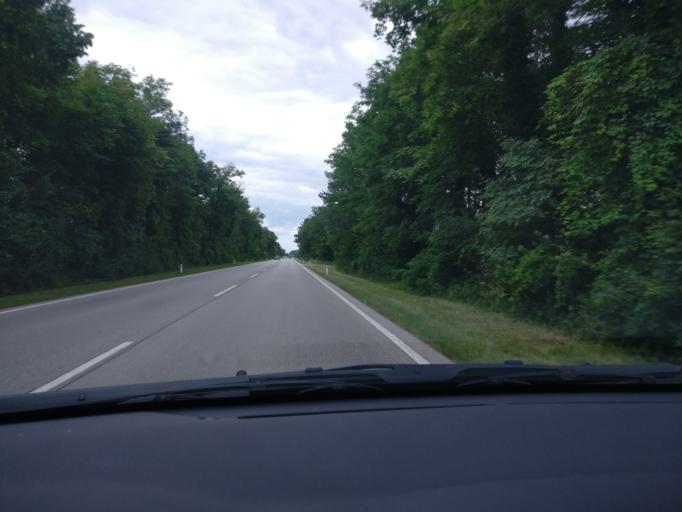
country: AT
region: Lower Austria
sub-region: Wiener Neustadt Stadt
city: Wiener Neustadt
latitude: 47.7729
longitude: 16.2236
